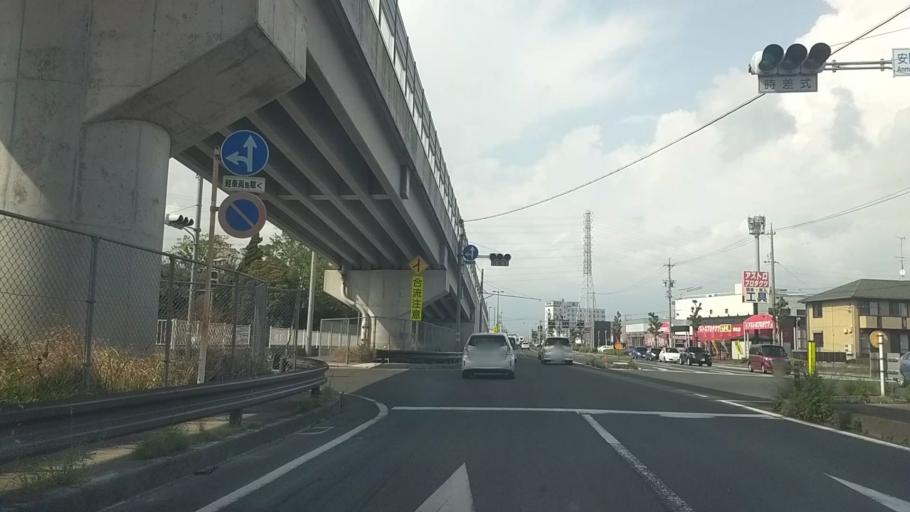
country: JP
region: Shizuoka
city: Hamamatsu
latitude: 34.7300
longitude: 137.7868
